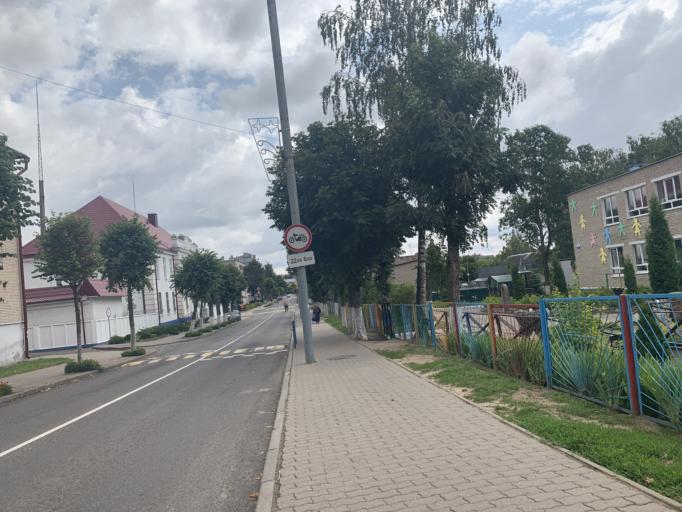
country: BY
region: Minsk
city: Nyasvizh
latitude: 53.2221
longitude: 26.6718
